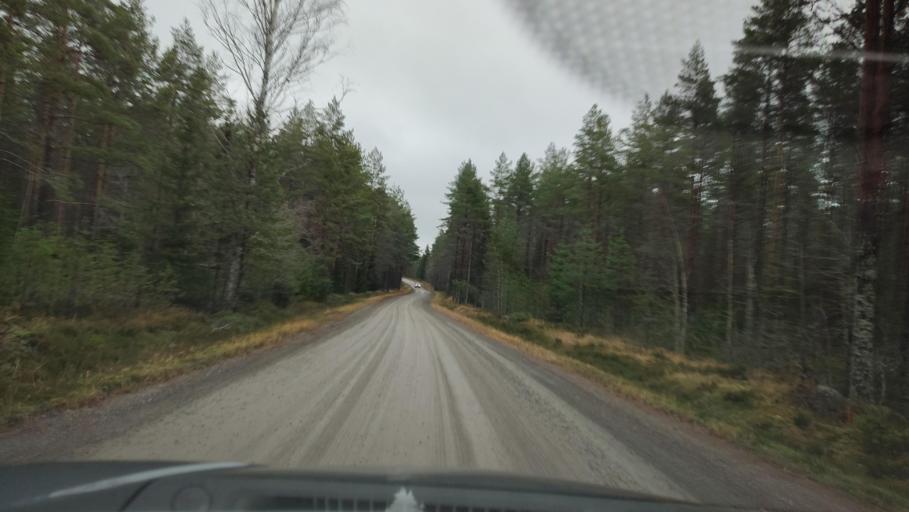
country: FI
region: Southern Ostrobothnia
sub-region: Suupohja
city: Karijoki
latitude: 62.1338
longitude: 21.6316
